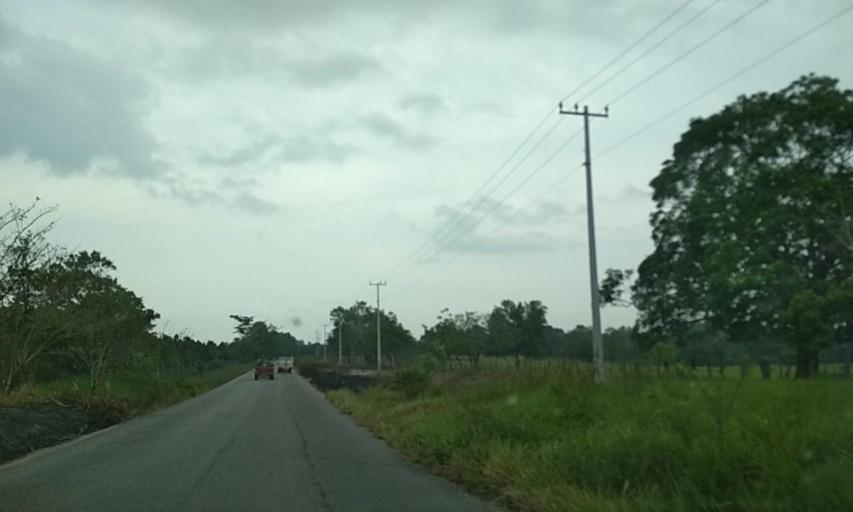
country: MX
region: Veracruz
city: Las Choapas
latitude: 17.8159
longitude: -94.1102
